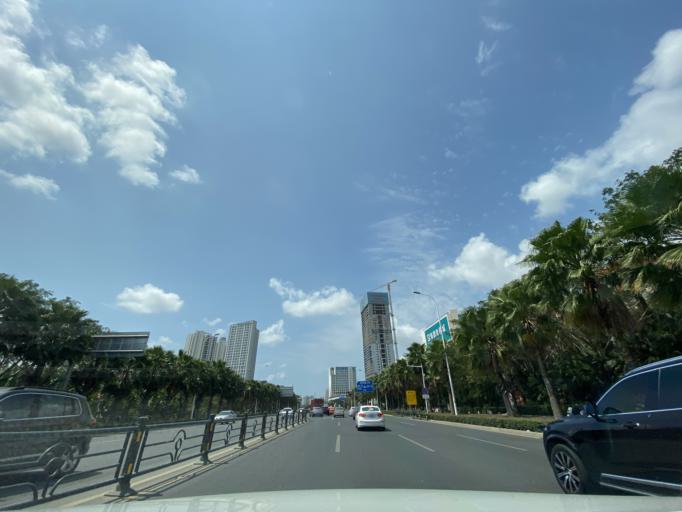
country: CN
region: Hainan
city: Sanya
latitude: 18.2916
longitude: 109.5270
